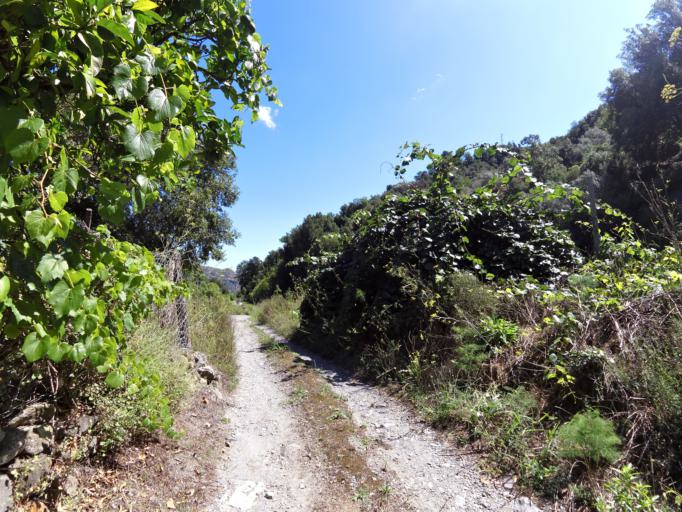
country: IT
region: Calabria
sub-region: Provincia di Reggio Calabria
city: Pazzano
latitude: 38.4751
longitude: 16.4386
